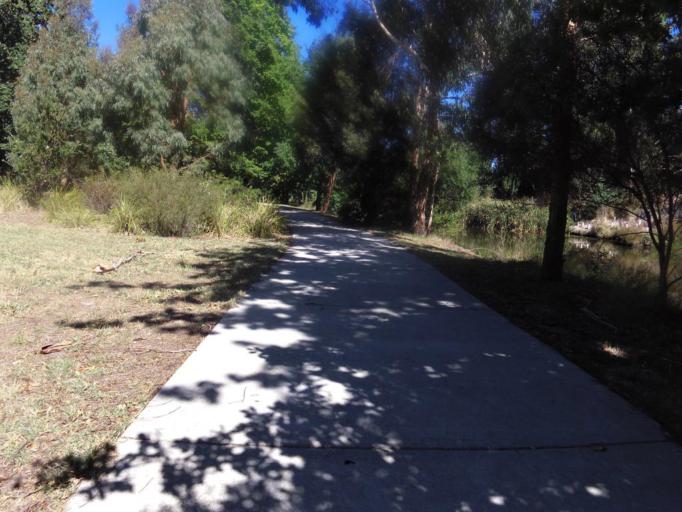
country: AU
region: Victoria
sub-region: Mount Alexander
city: Castlemaine
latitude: -37.2422
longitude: 144.4407
